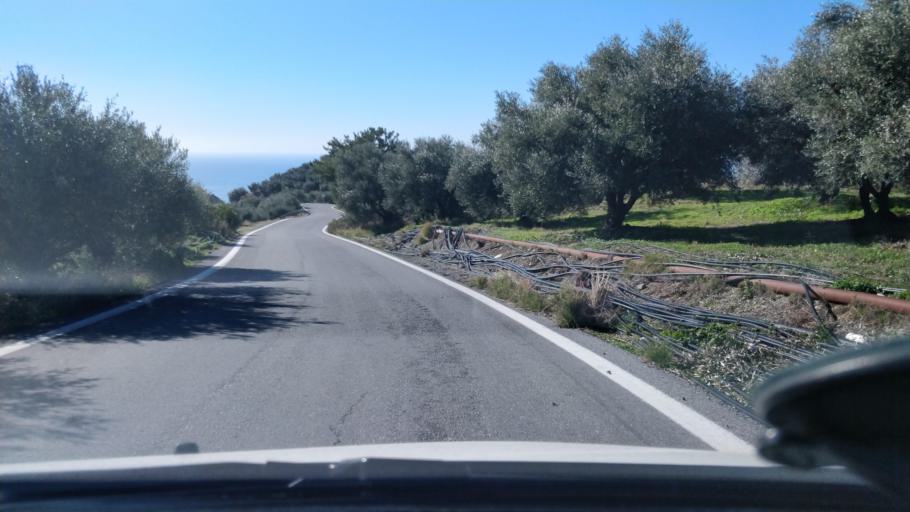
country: GR
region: Crete
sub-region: Nomos Irakleiou
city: Arkalochori
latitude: 35.0103
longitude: 25.4434
